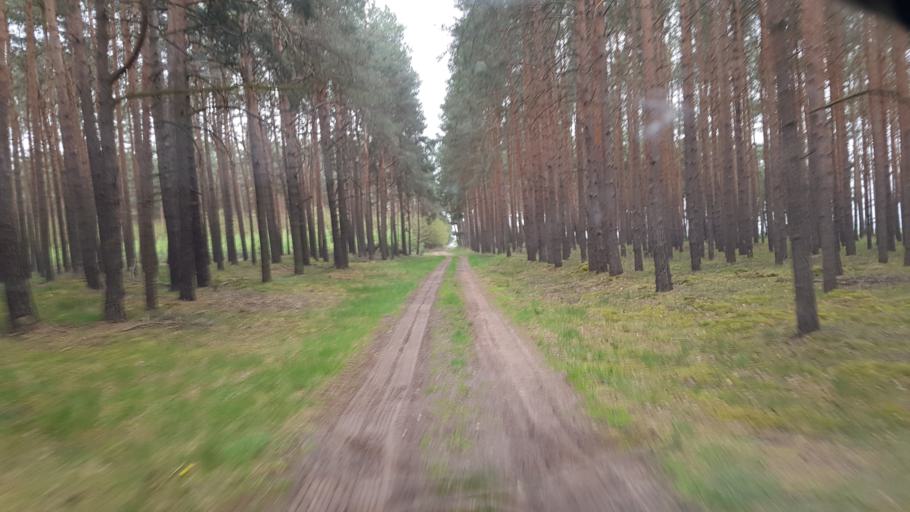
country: DE
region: Brandenburg
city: Schonewalde
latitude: 51.7060
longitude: 13.5620
